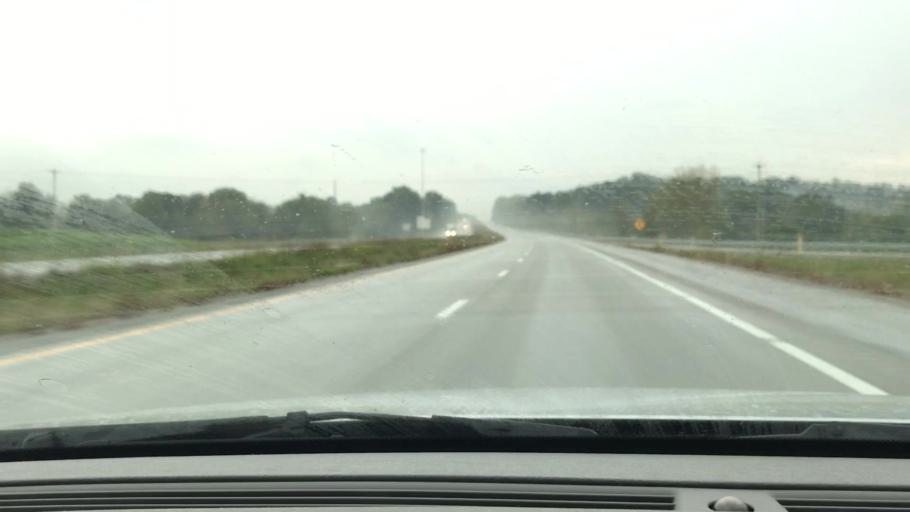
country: US
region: Kentucky
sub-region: Barren County
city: Glasgow
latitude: 36.9920
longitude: -85.9784
